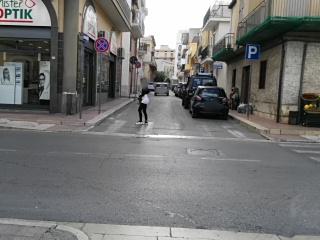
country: IT
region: Apulia
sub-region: Provincia di Bari
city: Triggiano
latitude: 41.0646
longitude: 16.9191
